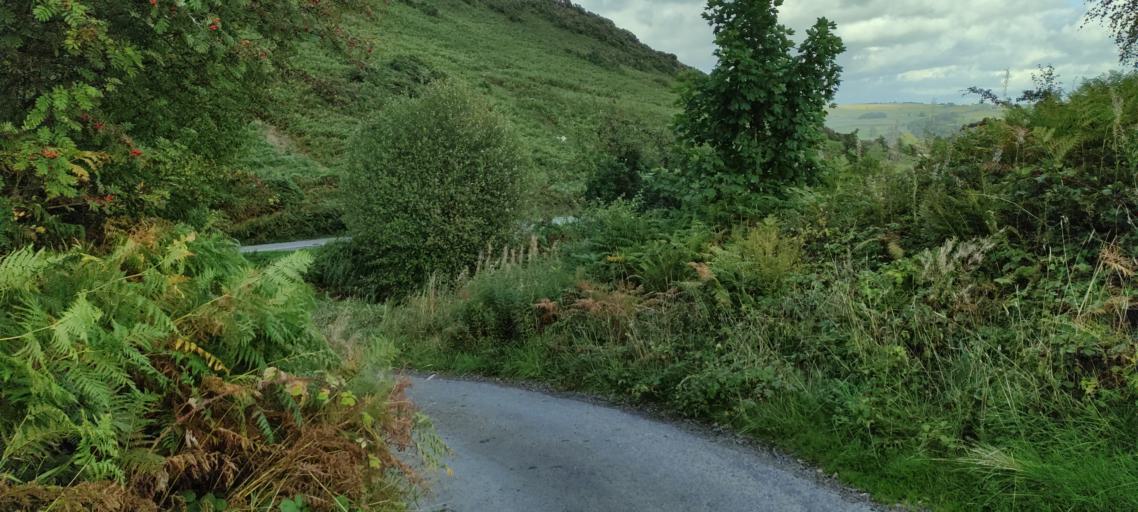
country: GB
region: England
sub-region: Cumbria
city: Keswick
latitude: 54.6357
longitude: -3.0105
